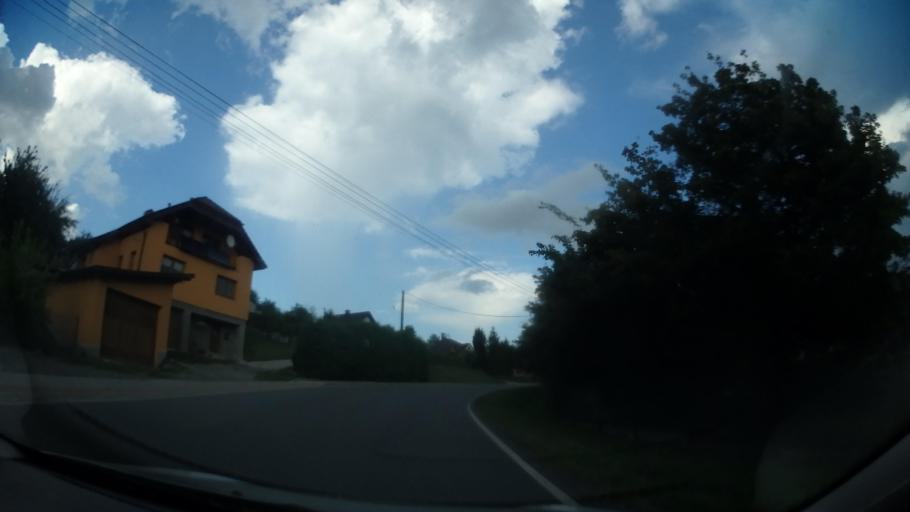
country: CZ
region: Olomoucky
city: Zabreh
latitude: 49.8834
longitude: 16.8022
